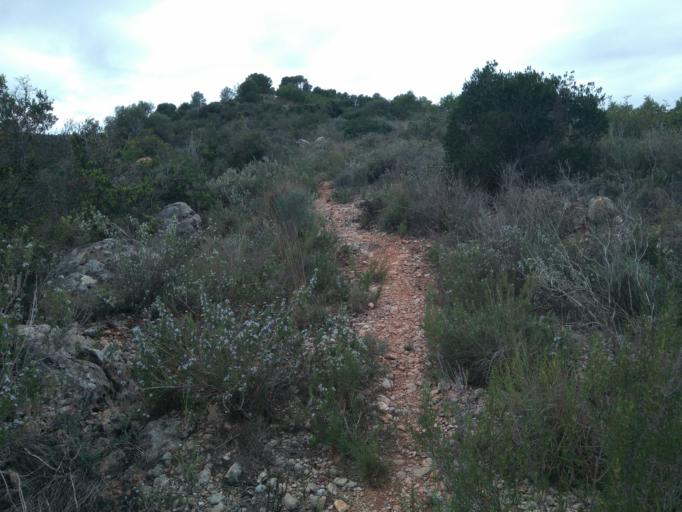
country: ES
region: Valencia
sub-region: Provincia de Valencia
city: Benimodo
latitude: 39.1973
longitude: -0.5748
